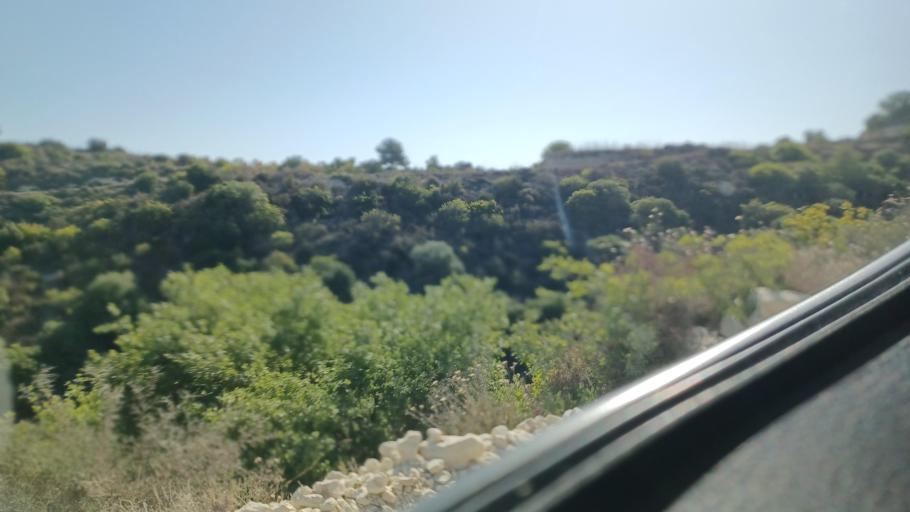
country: CY
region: Pafos
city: Tala
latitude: 34.8692
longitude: 32.4485
